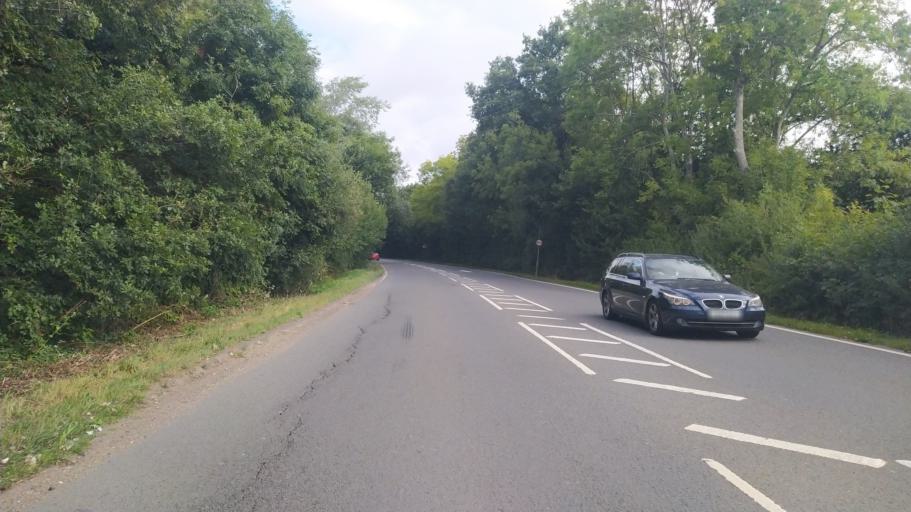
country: GB
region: England
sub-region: Hampshire
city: Totton
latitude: 50.9076
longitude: -1.4873
